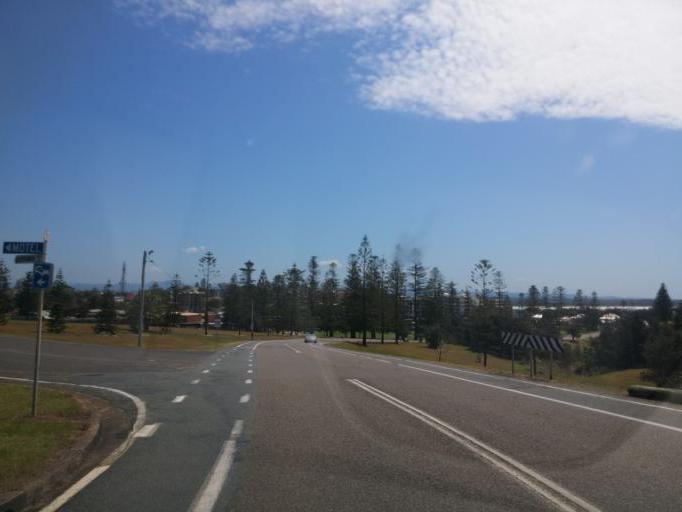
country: AU
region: New South Wales
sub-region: Port Macquarie-Hastings
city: Port Macquarie
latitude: -31.4346
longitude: 152.9241
